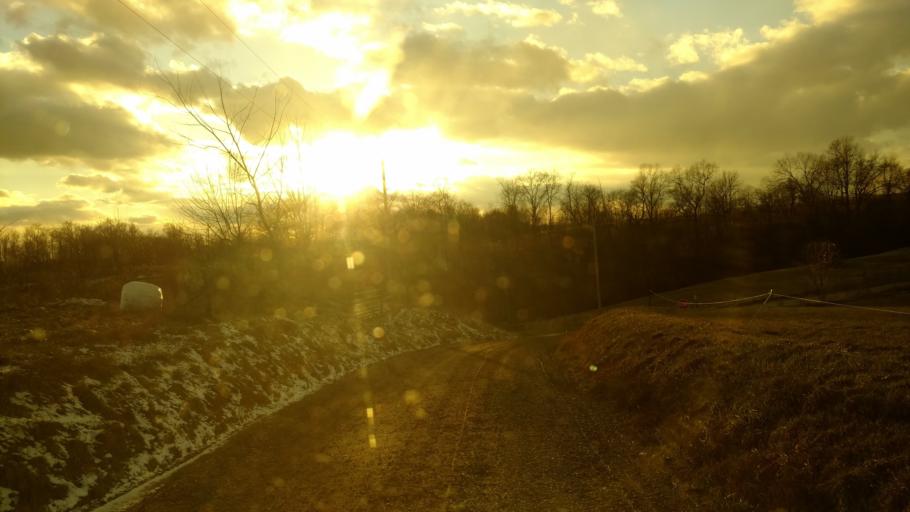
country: US
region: Ohio
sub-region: Tuscarawas County
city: Sugarcreek
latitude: 40.5162
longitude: -81.7796
